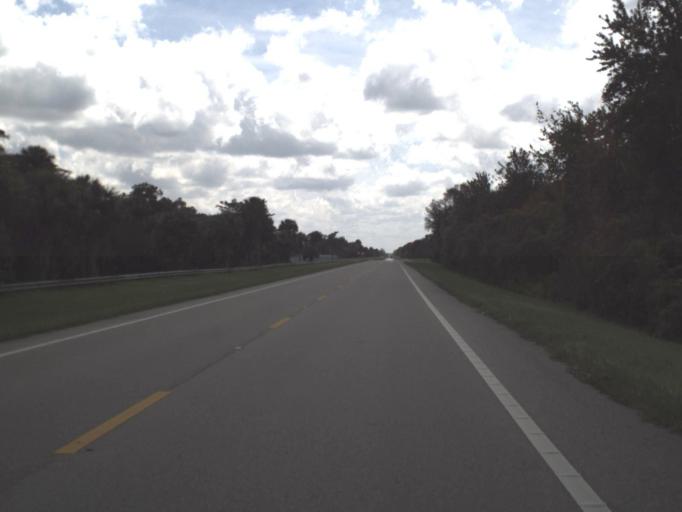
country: US
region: Florida
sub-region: Collier County
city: Immokalee
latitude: 26.3066
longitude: -81.3428
